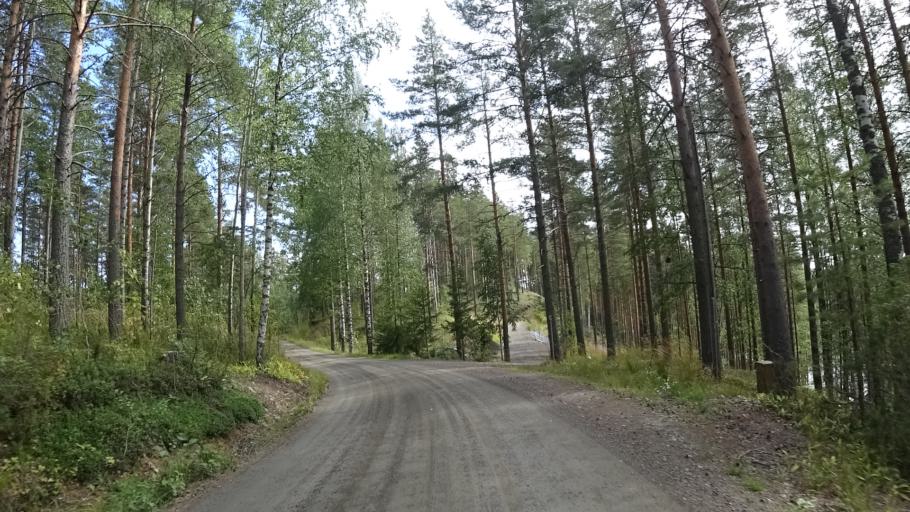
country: FI
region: North Karelia
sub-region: Joensuu
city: Pyhaeselkae
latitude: 62.3742
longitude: 29.8179
